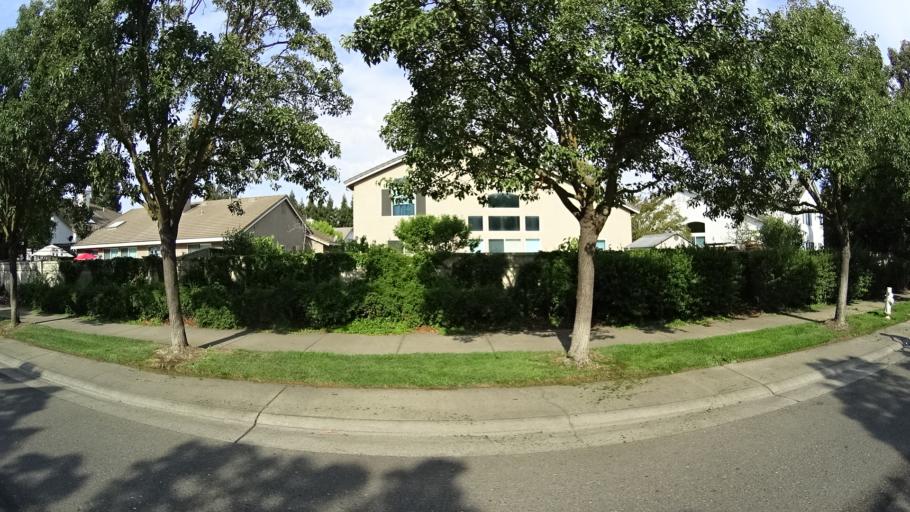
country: US
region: California
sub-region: Sacramento County
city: Laguna
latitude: 38.4155
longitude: -121.4588
